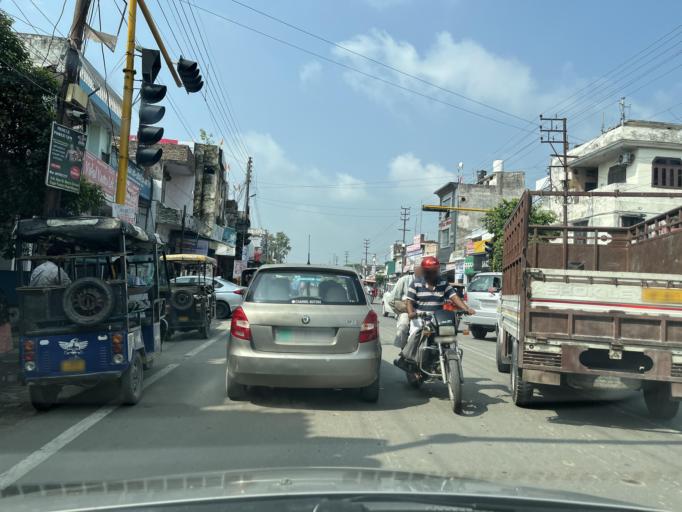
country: IN
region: Uttarakhand
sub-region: Udham Singh Nagar
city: Bazpur
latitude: 29.1610
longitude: 79.1539
